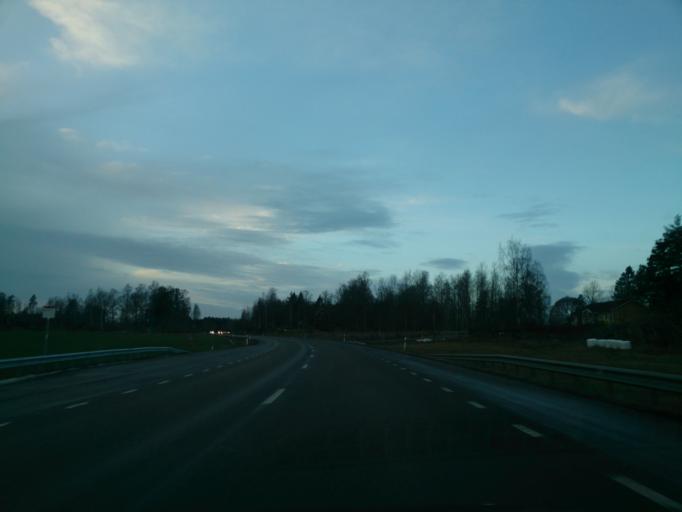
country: SE
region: OEstergoetland
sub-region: Atvidabergs Kommun
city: Atvidaberg
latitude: 58.2346
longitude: 15.9583
